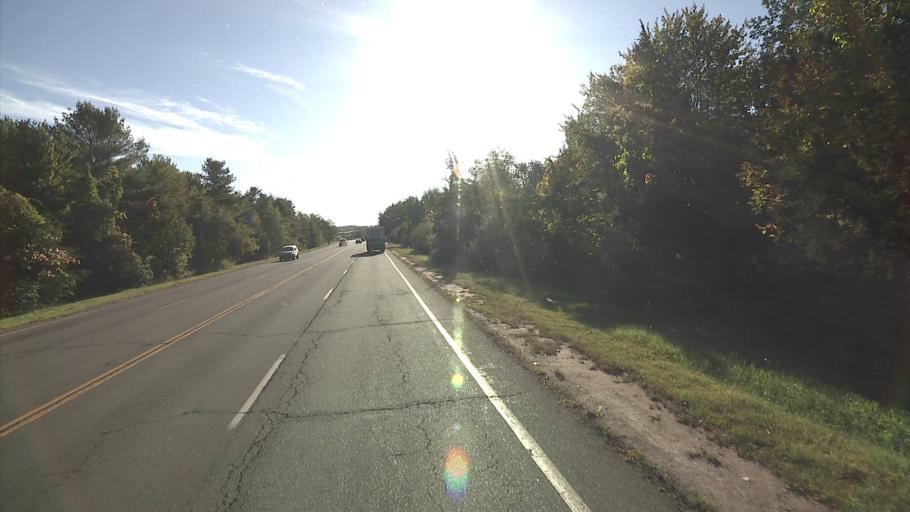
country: US
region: Connecticut
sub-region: New Haven County
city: Wallingford
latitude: 41.4828
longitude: -72.7800
